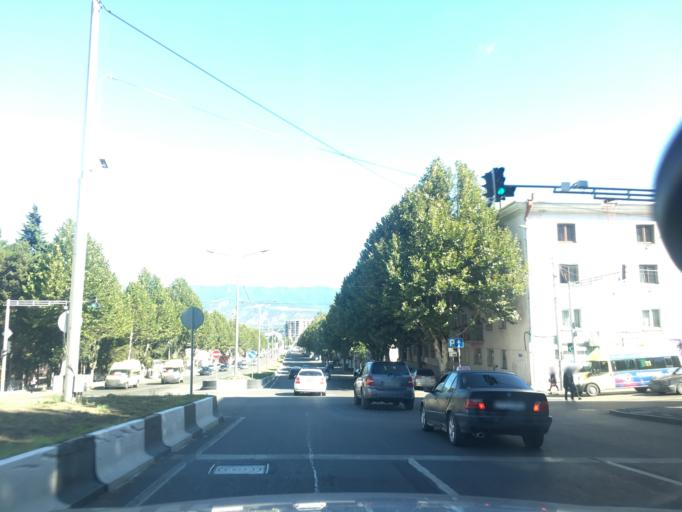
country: GE
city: Zahesi
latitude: 41.7743
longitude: 44.7948
